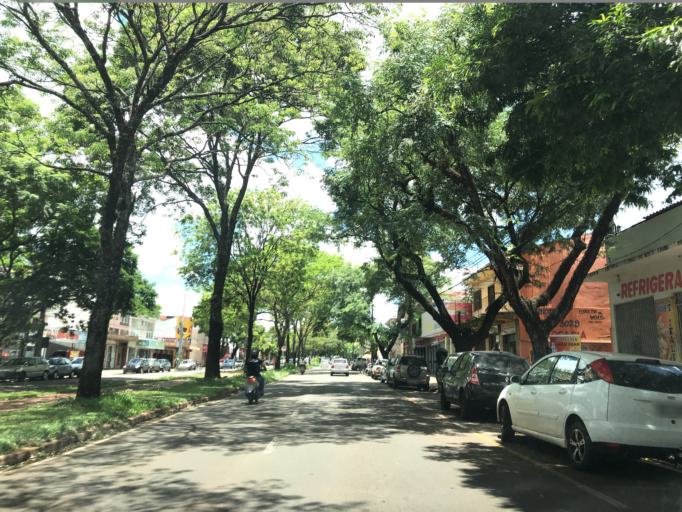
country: BR
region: Parana
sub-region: Maringa
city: Maringa
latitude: -23.3977
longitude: -51.9191
